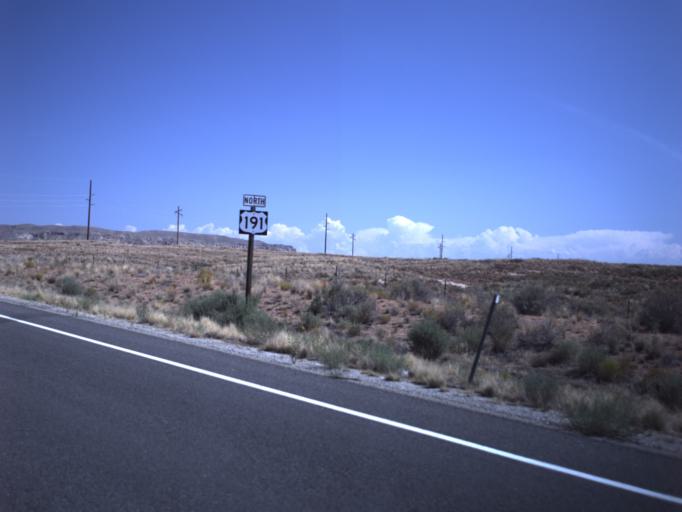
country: US
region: Utah
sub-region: San Juan County
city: Blanding
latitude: 37.3019
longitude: -109.5315
